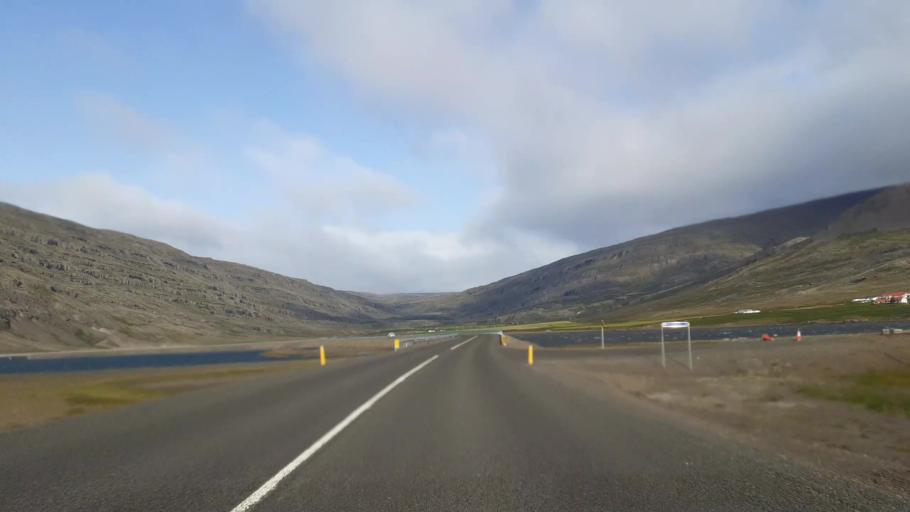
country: IS
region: East
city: Reydarfjoerdur
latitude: 64.7892
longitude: -14.4736
